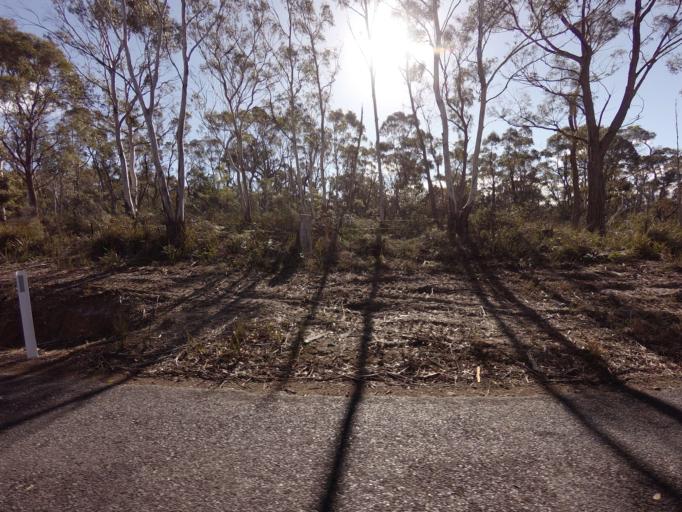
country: AU
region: Tasmania
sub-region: Sorell
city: Sorell
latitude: -42.3591
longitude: 147.9603
